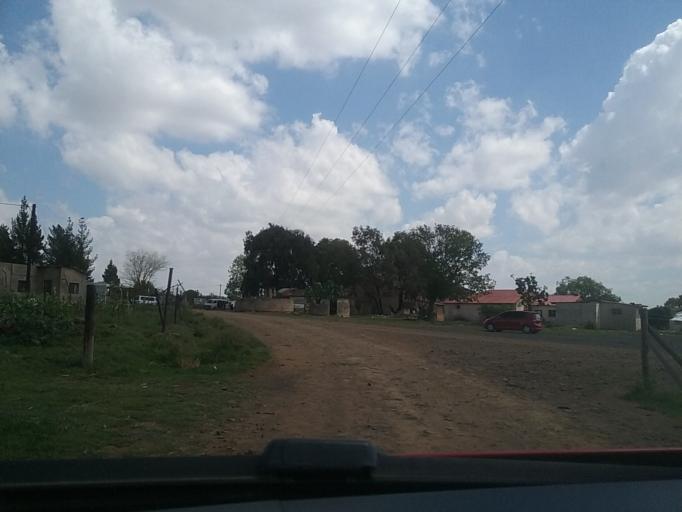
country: LS
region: Berea
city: Teyateyaneng
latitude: -29.2084
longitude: 27.8353
